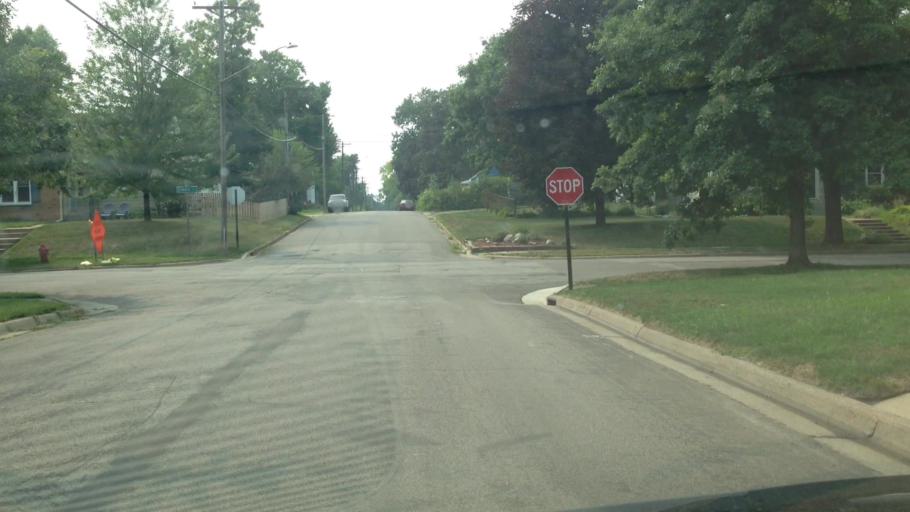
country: US
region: Minnesota
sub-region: Hennepin County
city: Saint Louis Park
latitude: 44.9515
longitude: -93.3602
